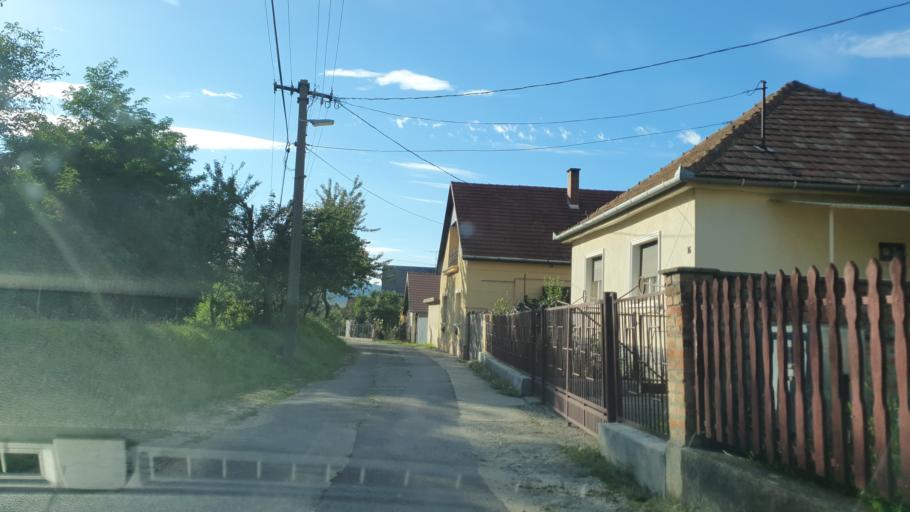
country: HU
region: Nograd
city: Tar
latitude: 47.9471
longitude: 19.7406
